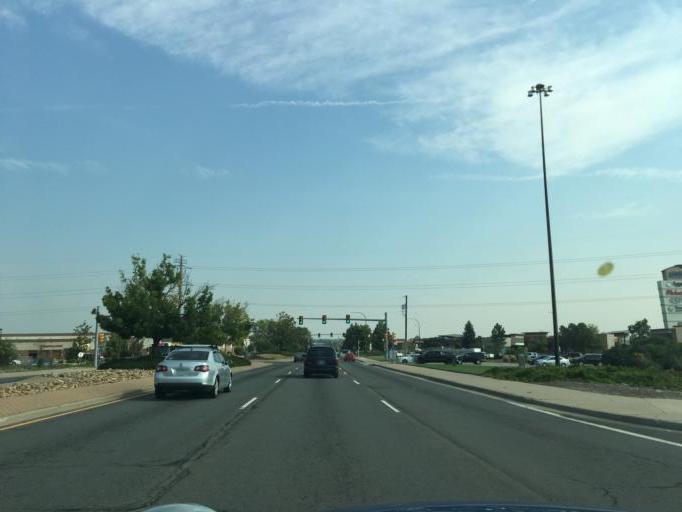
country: US
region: Colorado
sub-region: Jefferson County
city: Arvada
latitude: 39.7873
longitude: -105.0814
